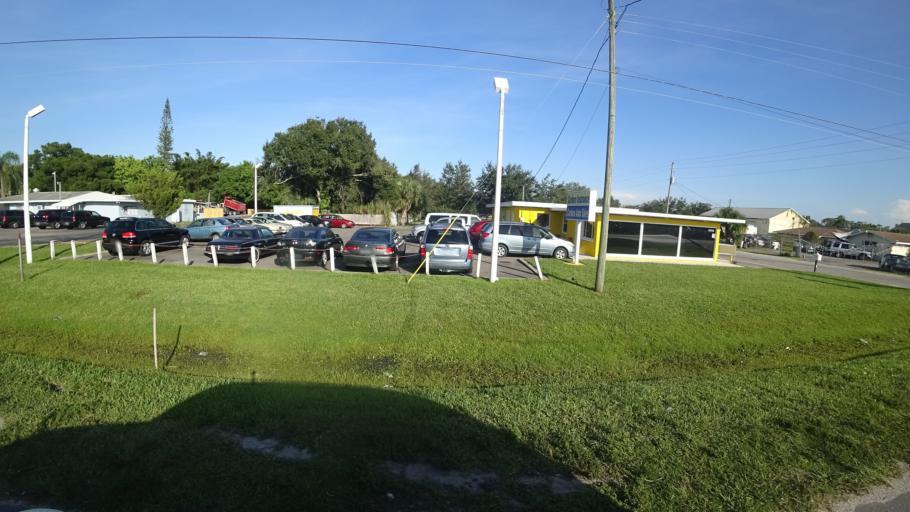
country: US
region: Florida
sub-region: Manatee County
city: Samoset
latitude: 27.4437
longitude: -82.5466
